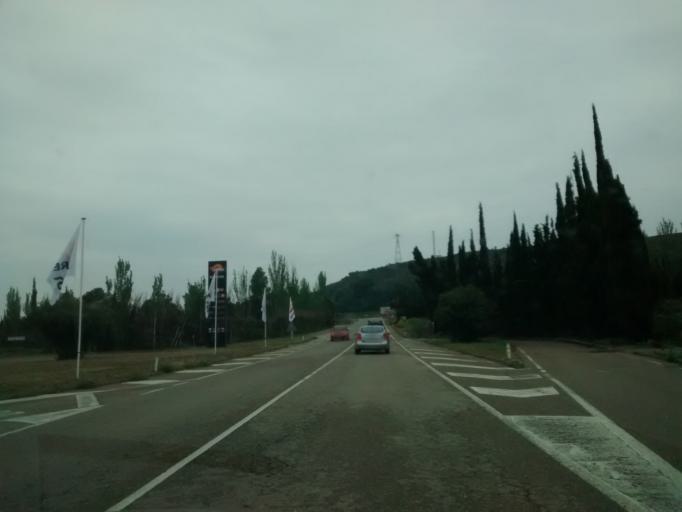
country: ES
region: Aragon
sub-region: Provincia de Zaragoza
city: Caspe
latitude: 41.2491
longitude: -0.0685
